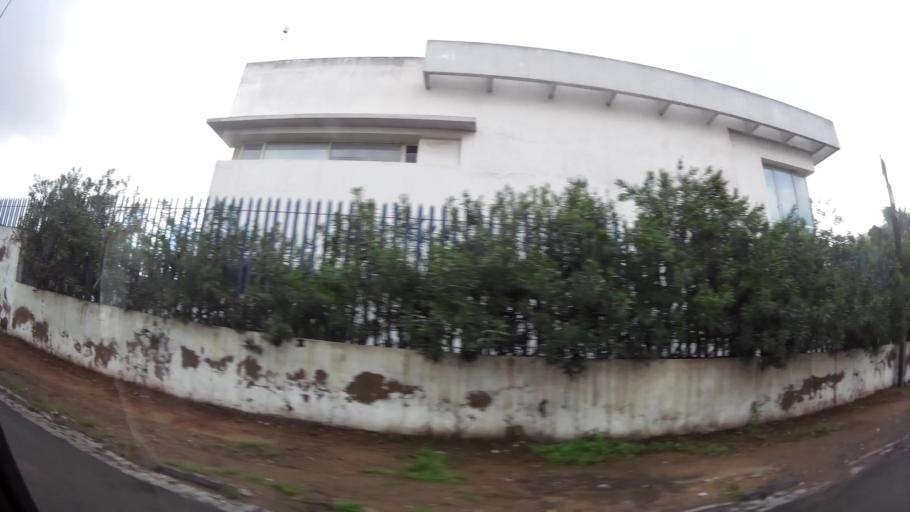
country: MA
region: Grand Casablanca
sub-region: Mediouna
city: Tit Mellil
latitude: 33.5905
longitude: -7.5431
